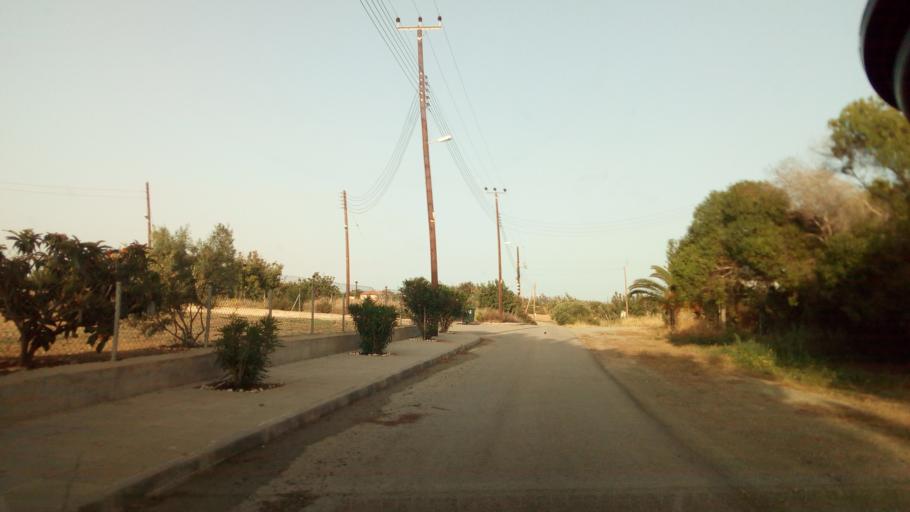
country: CY
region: Larnaka
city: Tersefanou
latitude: 34.8048
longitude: 33.5062
